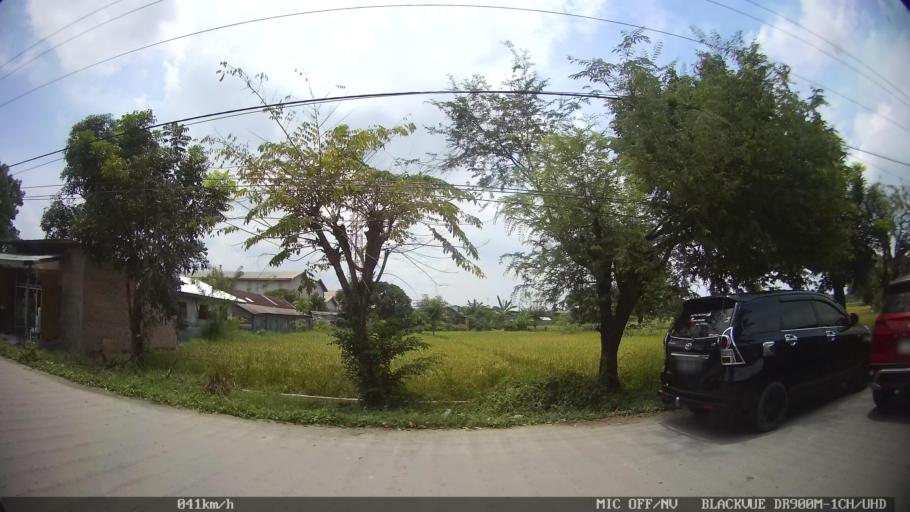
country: ID
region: North Sumatra
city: Labuhan Deli
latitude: 3.6891
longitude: 98.6856
